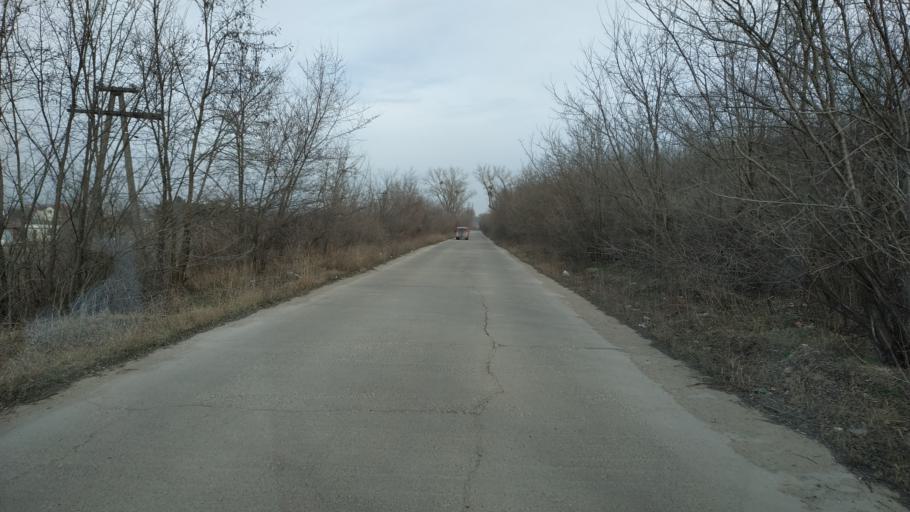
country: MD
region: Chisinau
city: Vatra
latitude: 47.0831
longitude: 28.7415
